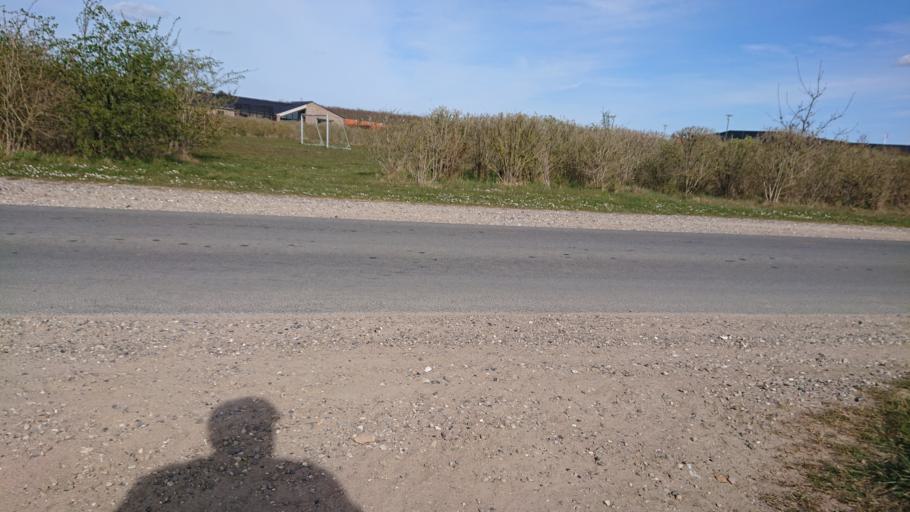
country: DK
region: South Denmark
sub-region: Nyborg Kommune
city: Nyborg
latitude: 55.3060
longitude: 10.7514
